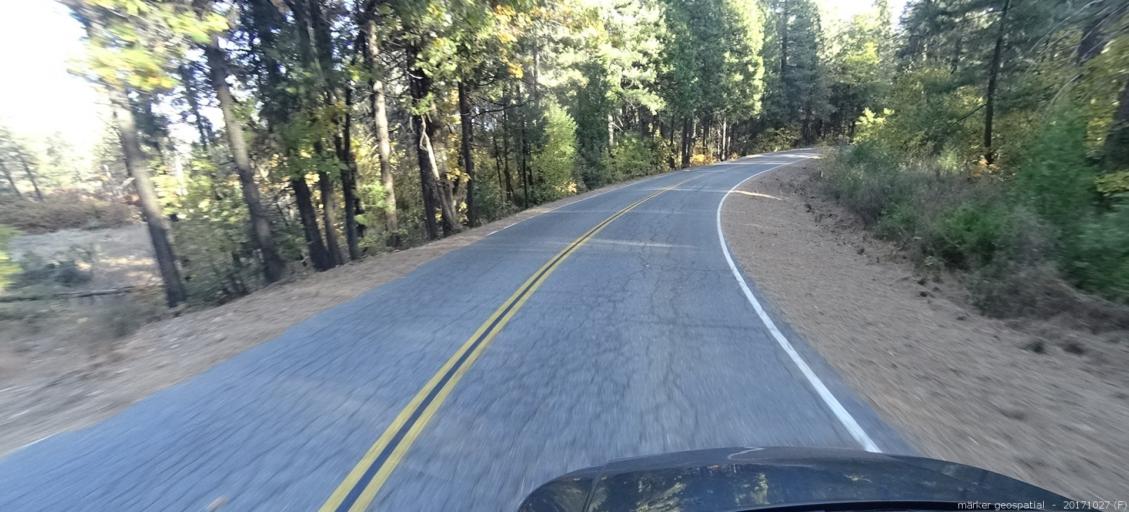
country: US
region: California
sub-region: Shasta County
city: Burney
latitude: 40.9971
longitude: -121.9200
